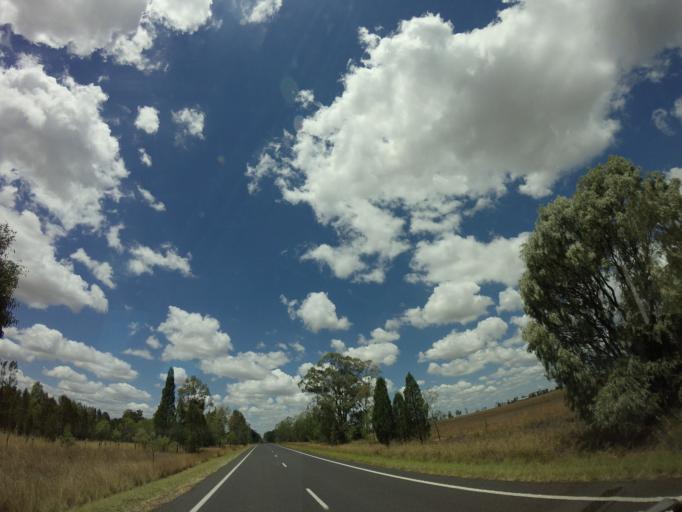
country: AU
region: Queensland
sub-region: Toowoomba
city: Oakey
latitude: -27.9030
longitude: 151.1952
